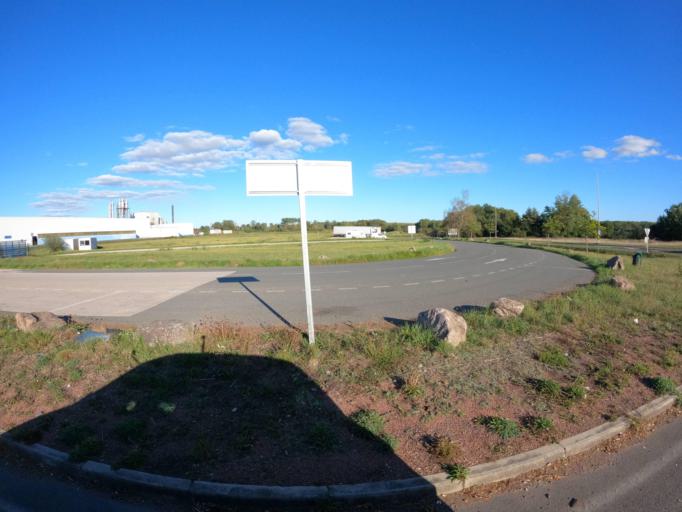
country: FR
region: Bourgogne
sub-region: Departement de Saone-et-Loire
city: Torcy
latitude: 46.7555
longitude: 4.4407
